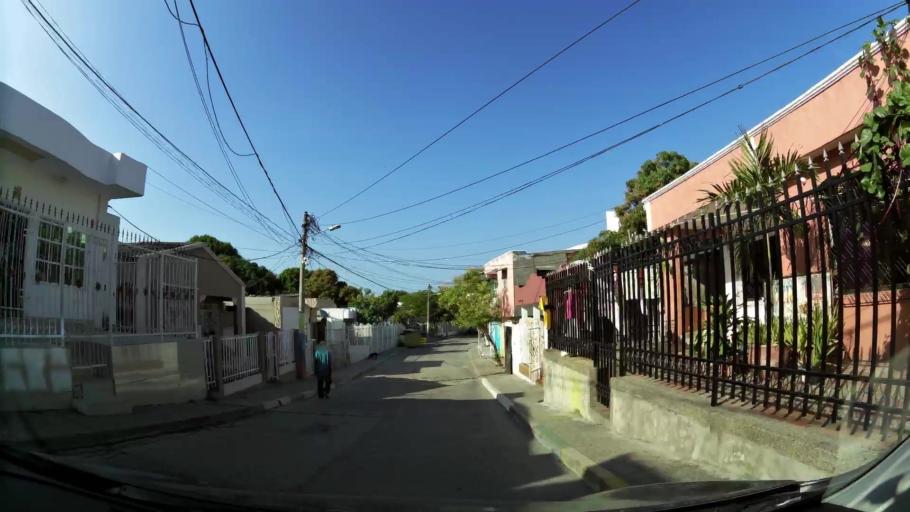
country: CO
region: Bolivar
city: Cartagena
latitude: 10.4035
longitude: -75.4862
